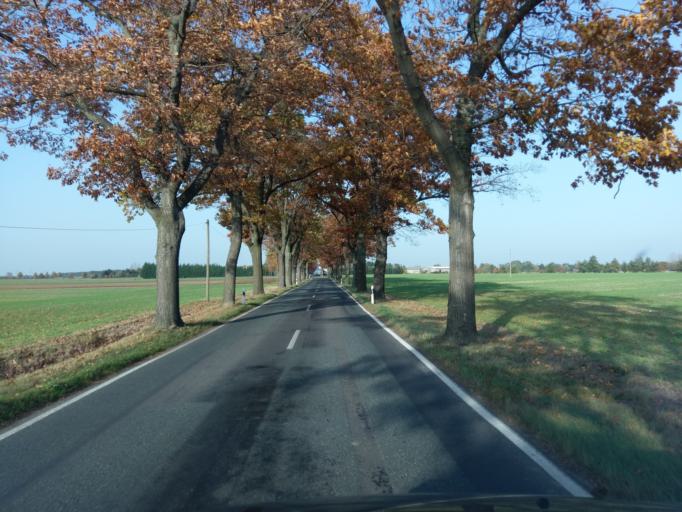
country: DE
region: Brandenburg
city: Falkenberg
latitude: 51.6283
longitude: 13.2320
